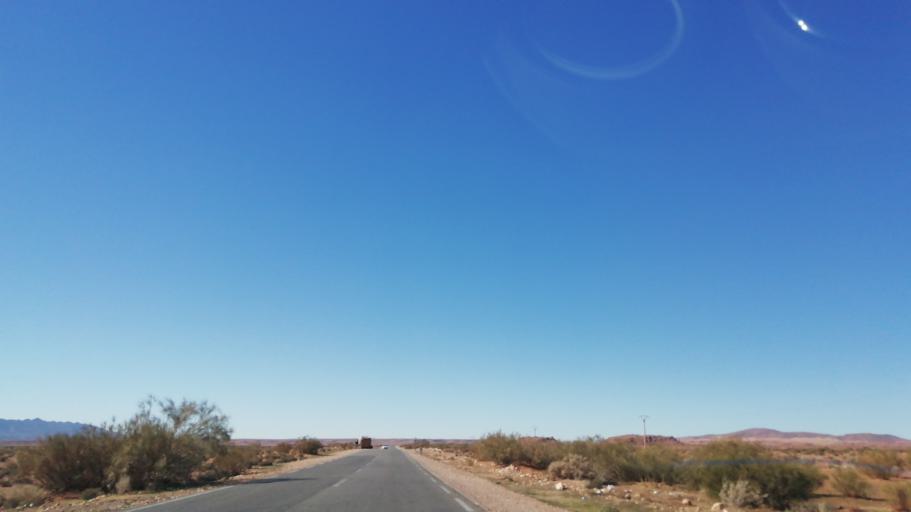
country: DZ
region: El Bayadh
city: El Abiodh Sidi Cheikh
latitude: 33.1815
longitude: 0.5490
